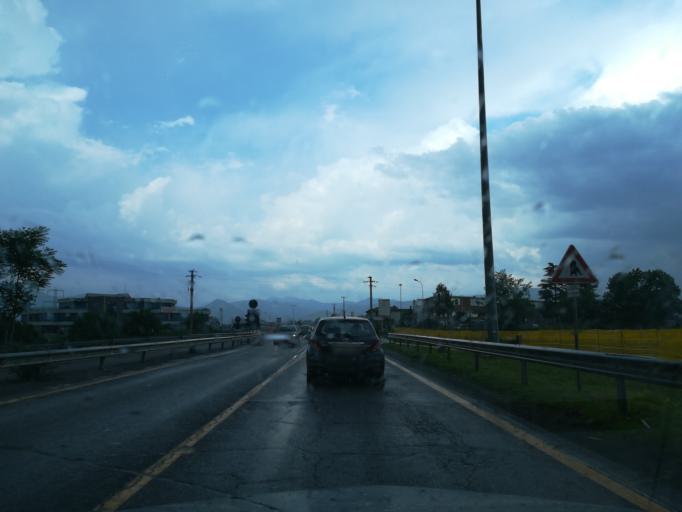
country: IT
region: Lombardy
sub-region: Provincia di Bergamo
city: Curno
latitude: 45.6821
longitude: 9.6018
